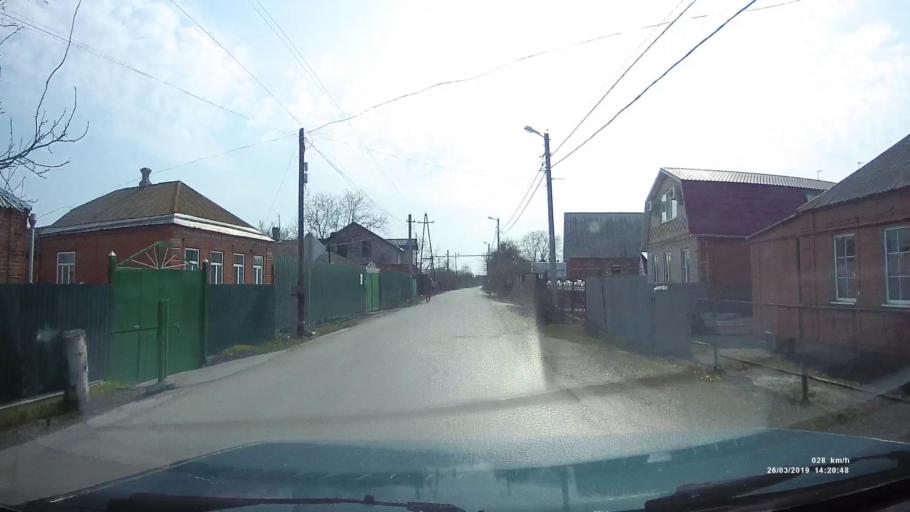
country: RU
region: Rostov
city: Novobessergenovka
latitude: 47.1889
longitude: 38.8701
